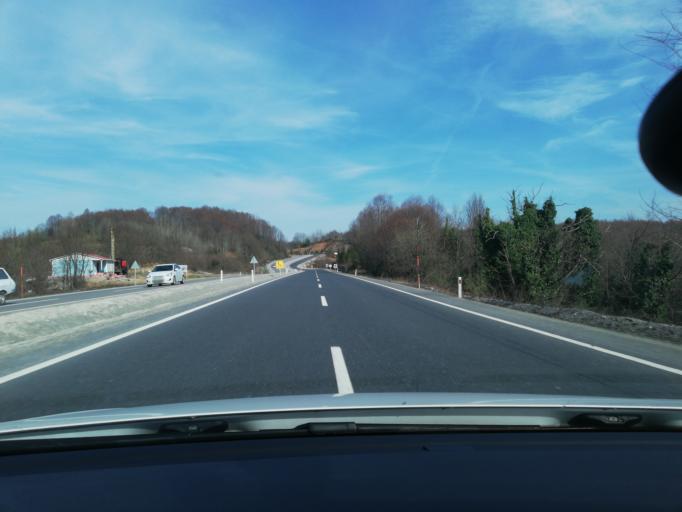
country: TR
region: Zonguldak
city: Kozlu
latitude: 41.3323
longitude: 31.6207
